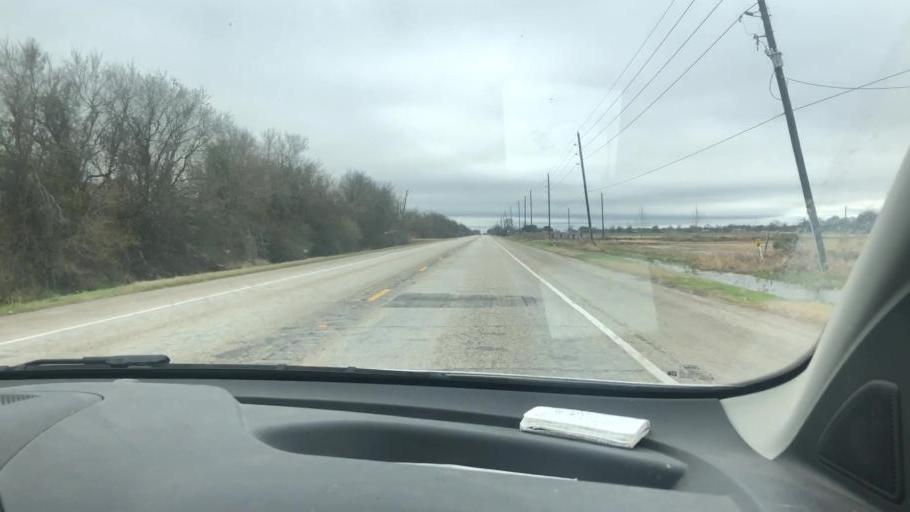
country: US
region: Texas
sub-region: Wharton County
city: Wharton
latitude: 29.2780
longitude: -96.0646
